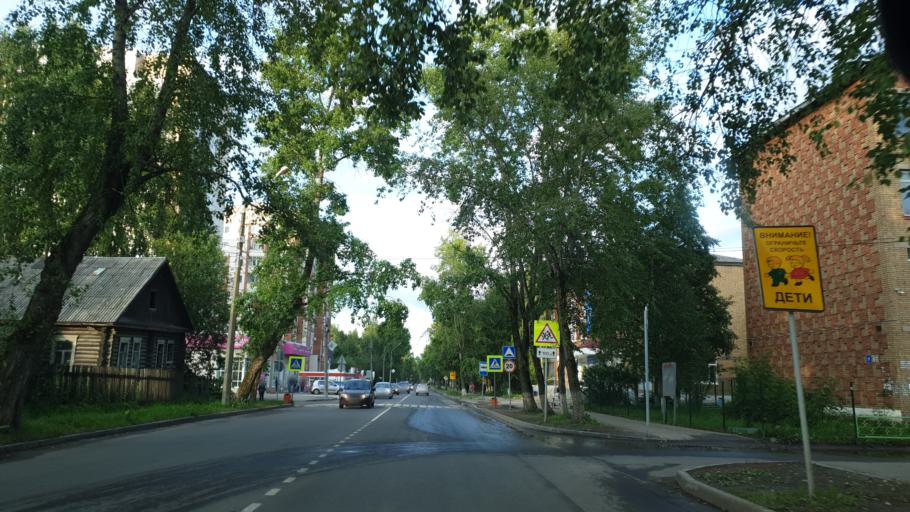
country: RU
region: Komi Republic
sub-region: Syktyvdinskiy Rayon
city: Syktyvkar
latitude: 61.6649
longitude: 50.7961
